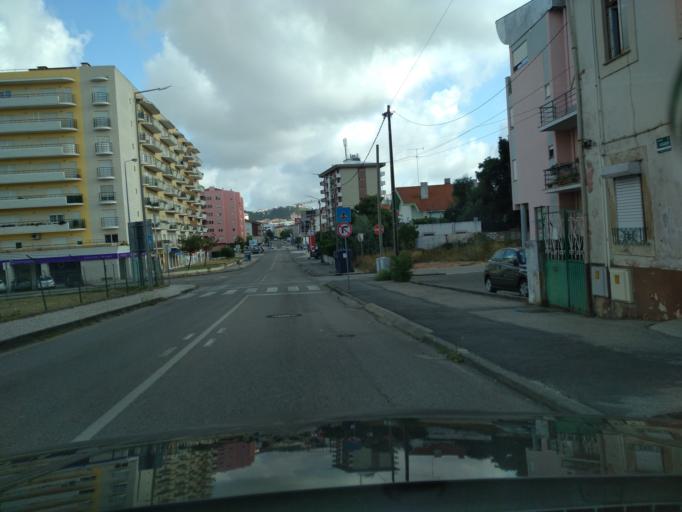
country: PT
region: Coimbra
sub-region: Coimbra
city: Coimbra
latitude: 40.1947
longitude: -8.4027
